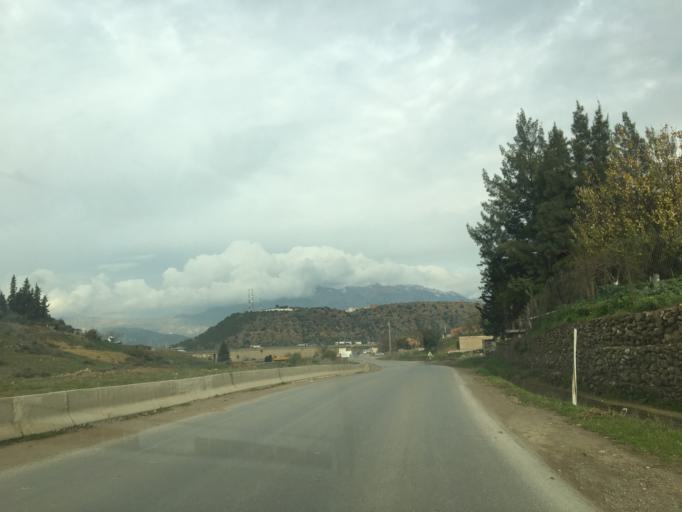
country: DZ
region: Bouira
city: Bouira
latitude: 36.3588
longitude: 3.8963
